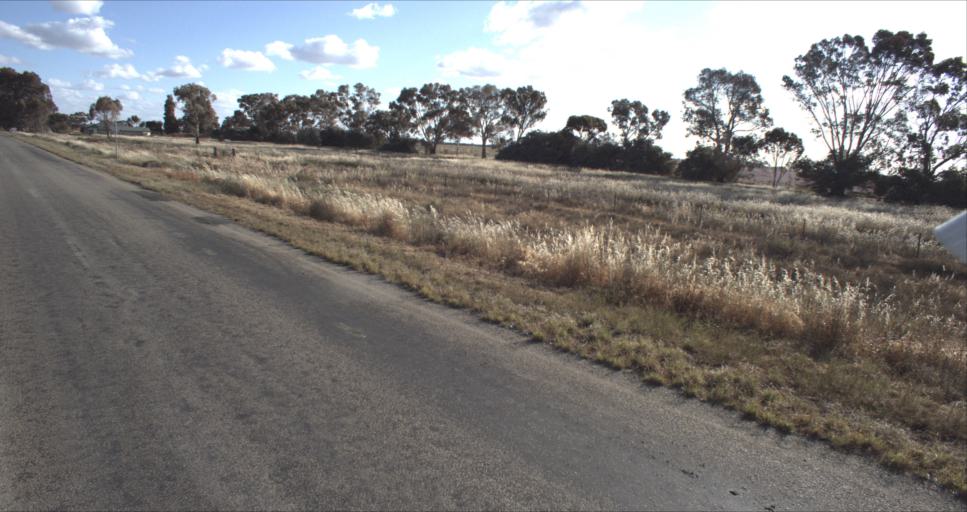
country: AU
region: New South Wales
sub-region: Leeton
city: Leeton
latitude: -34.5384
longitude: 146.2802
